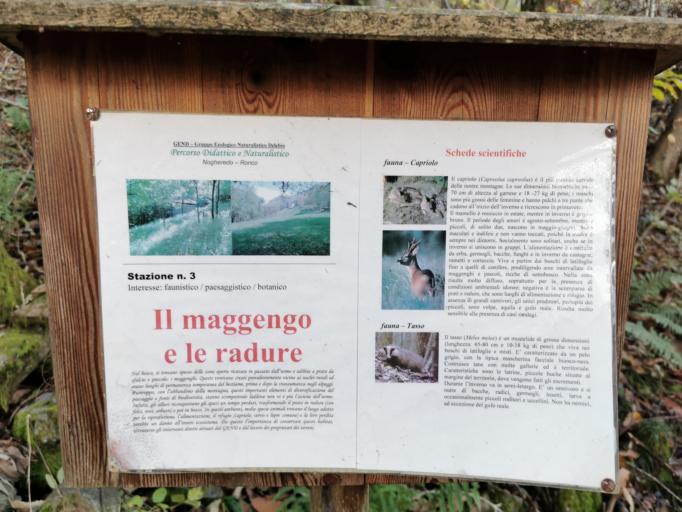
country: IT
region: Lombardy
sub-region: Provincia di Sondrio
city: Delebio
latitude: 46.1277
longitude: 9.4540
